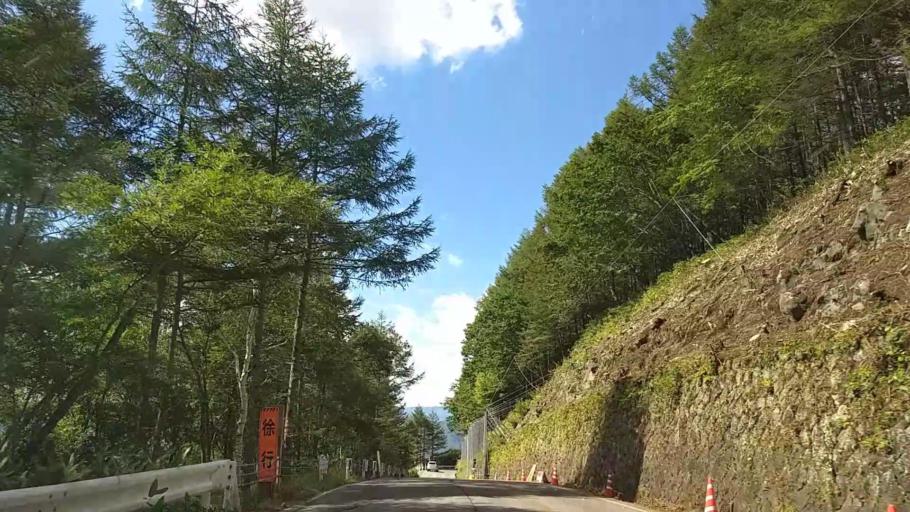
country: JP
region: Nagano
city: Chino
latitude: 36.0918
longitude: 138.2750
